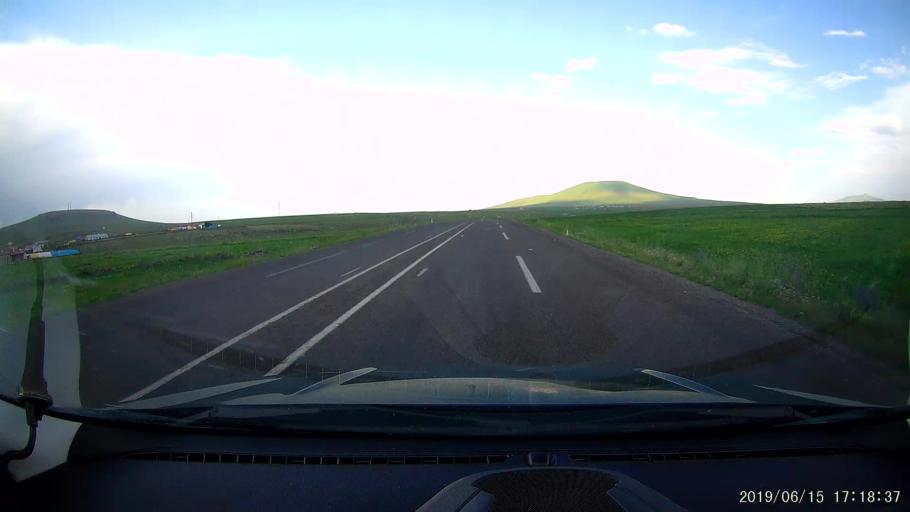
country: TR
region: Kars
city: Kars
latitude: 40.6130
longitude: 43.2619
